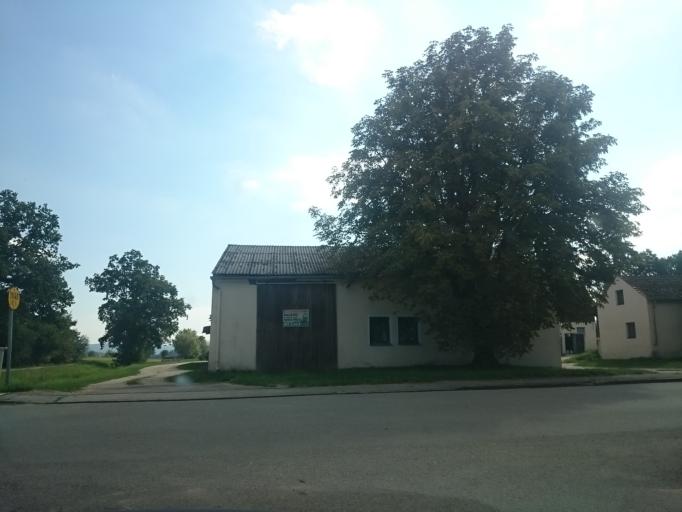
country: DE
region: Bavaria
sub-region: Upper Palatinate
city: Freystadt
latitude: 49.1498
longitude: 11.2746
